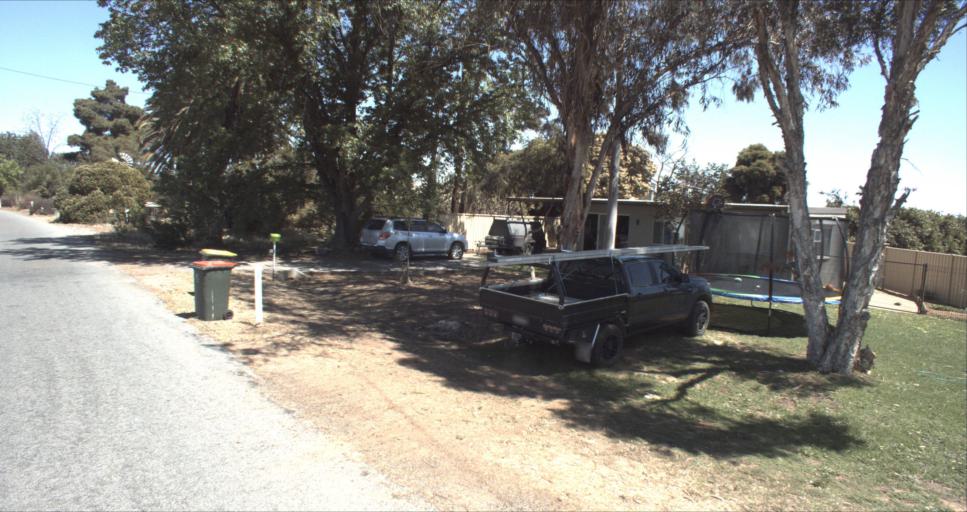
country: AU
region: New South Wales
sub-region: Leeton
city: Leeton
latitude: -34.5419
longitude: 146.3946
